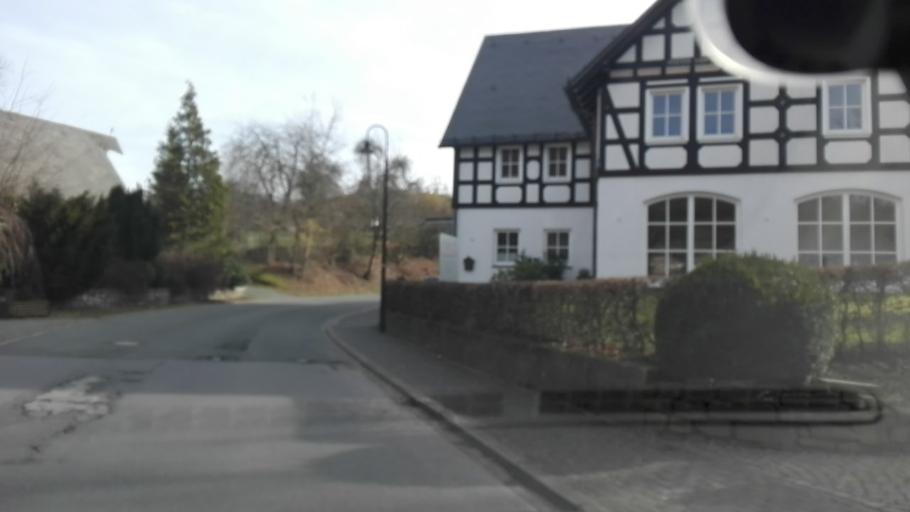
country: DE
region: North Rhine-Westphalia
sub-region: Regierungsbezirk Arnsberg
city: Schmallenberg
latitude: 51.1456
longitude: 8.3268
